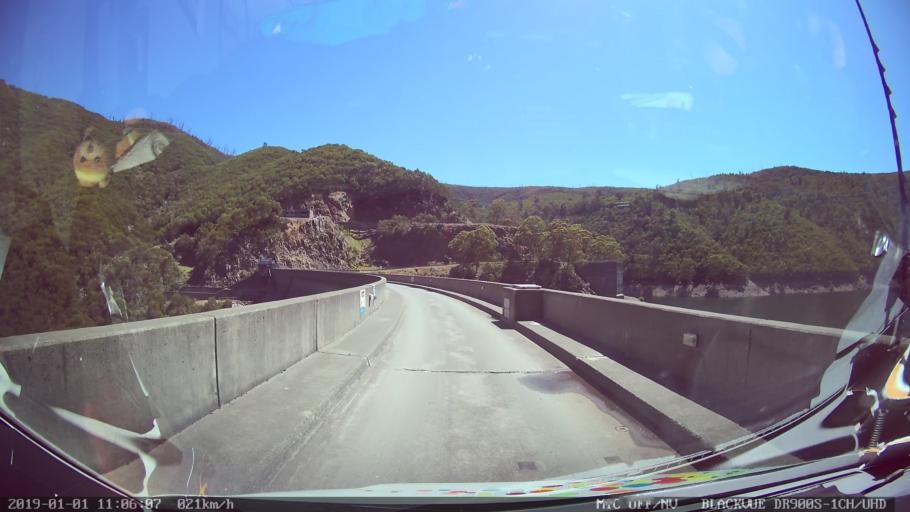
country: AU
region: New South Wales
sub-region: Snowy River
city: Jindabyne
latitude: -35.9652
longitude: 148.3897
